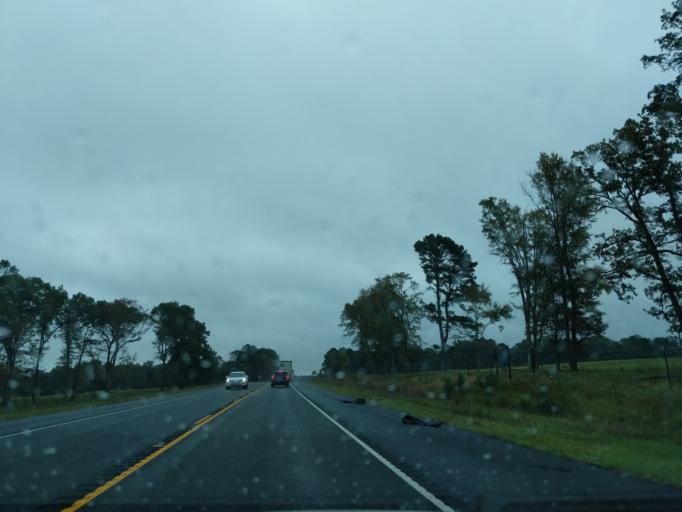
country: US
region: Louisiana
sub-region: Caddo Parish
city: Greenwood
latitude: 32.4353
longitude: -93.9838
